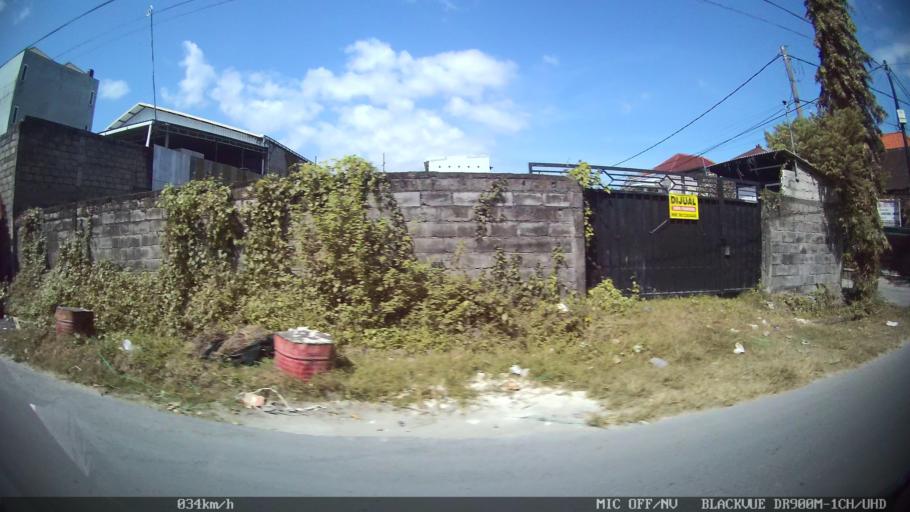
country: ID
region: Bali
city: Banjar Kertasari
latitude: -8.6410
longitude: 115.1794
